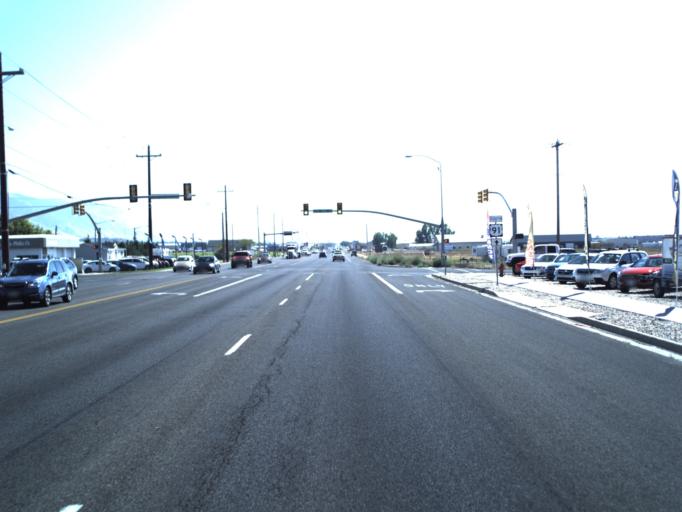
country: US
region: Utah
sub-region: Cache County
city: Hyde Park
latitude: 41.8000
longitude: -111.8336
